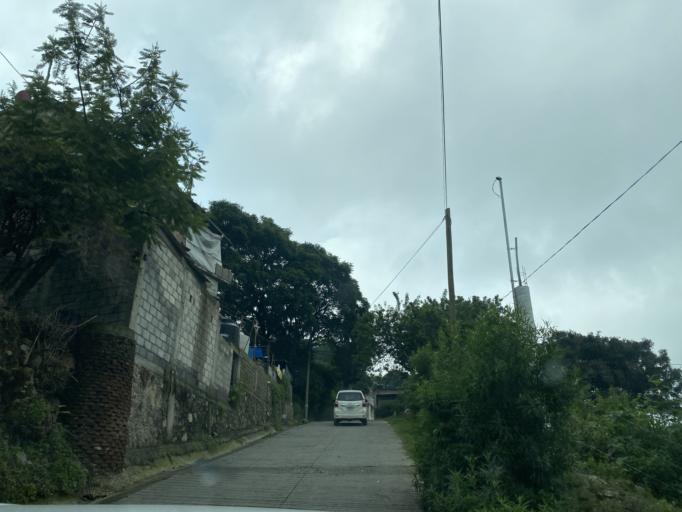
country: MX
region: Morelos
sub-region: Yecapixtla
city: Achichipico
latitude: 18.9519
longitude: -98.8266
